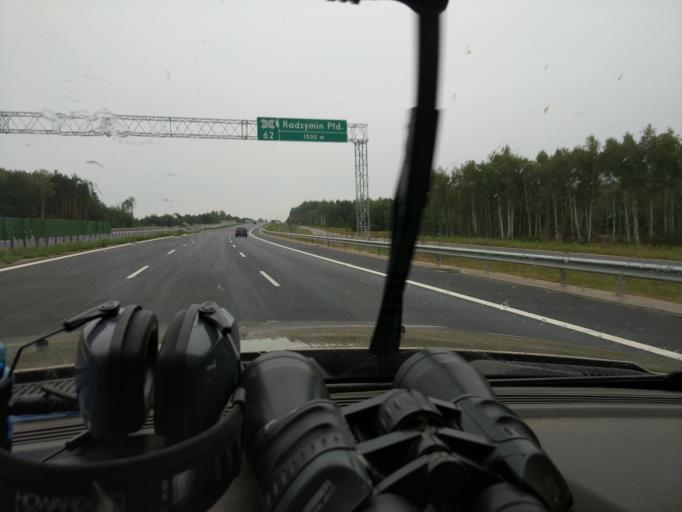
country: PL
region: Masovian Voivodeship
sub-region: Powiat wolominski
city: Slupno
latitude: 52.3800
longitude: 21.1892
